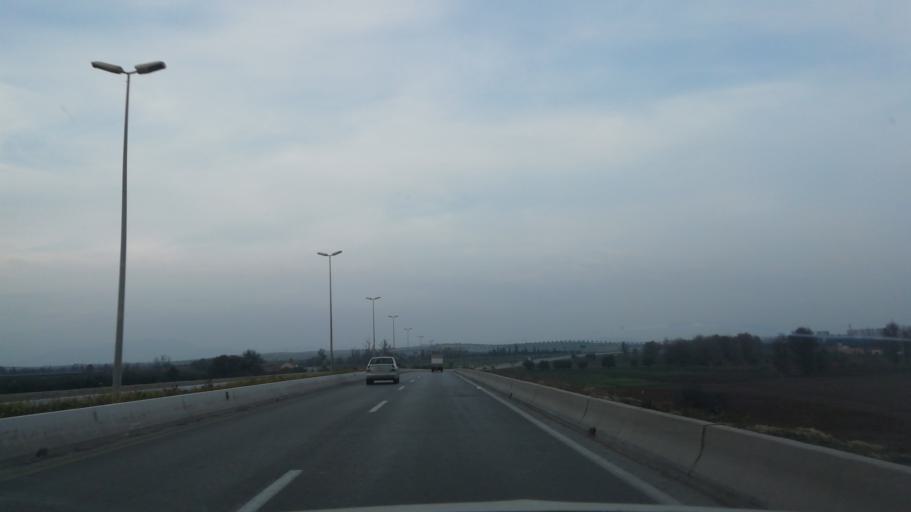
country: DZ
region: Sidi Bel Abbes
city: Sidi Bel Abbes
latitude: 35.1872
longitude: -0.6603
